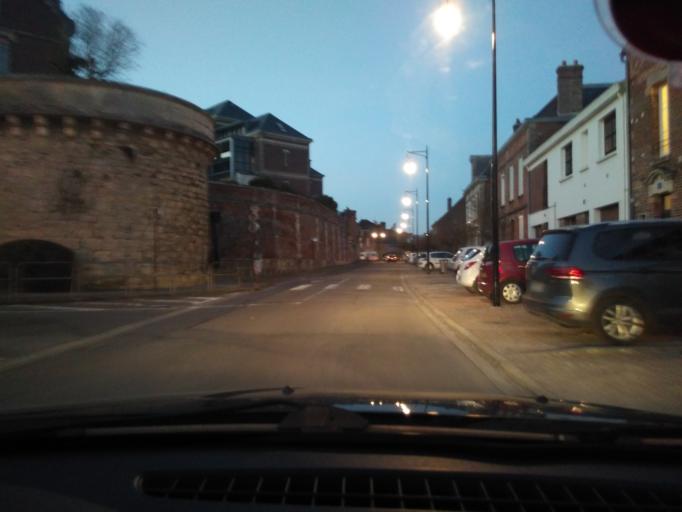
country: FR
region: Picardie
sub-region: Departement de l'Aisne
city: Laon
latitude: 49.5600
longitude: 3.6127
